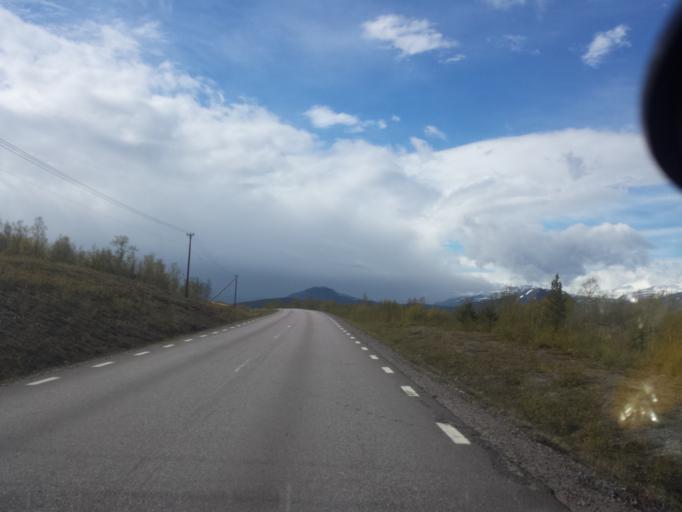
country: SE
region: Norrbotten
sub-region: Kiruna Kommun
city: Kiruna
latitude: 68.2157
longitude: 19.7396
